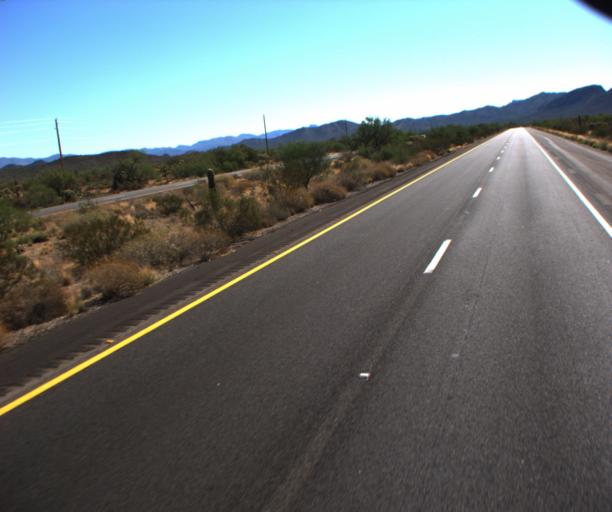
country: US
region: Arizona
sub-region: Pinal County
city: Gold Camp
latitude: 33.2575
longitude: -111.3132
